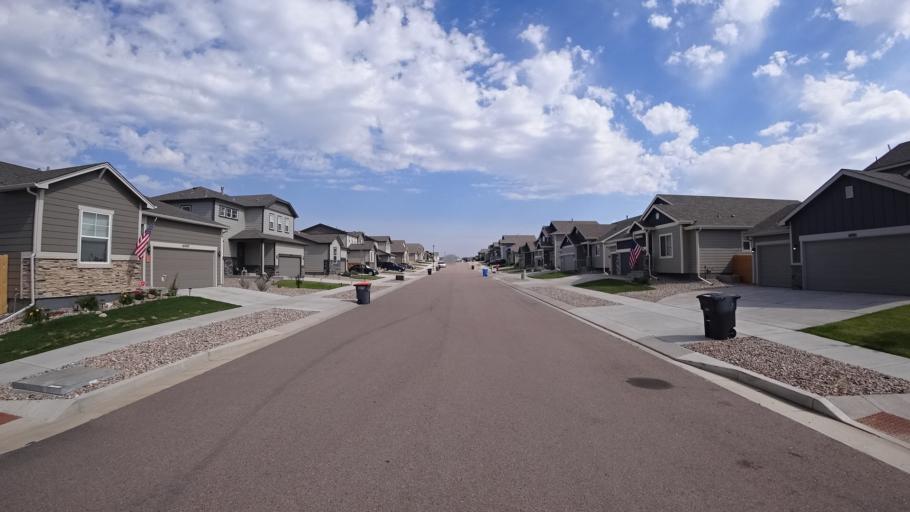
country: US
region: Colorado
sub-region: El Paso County
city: Cimarron Hills
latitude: 38.9190
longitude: -104.6810
